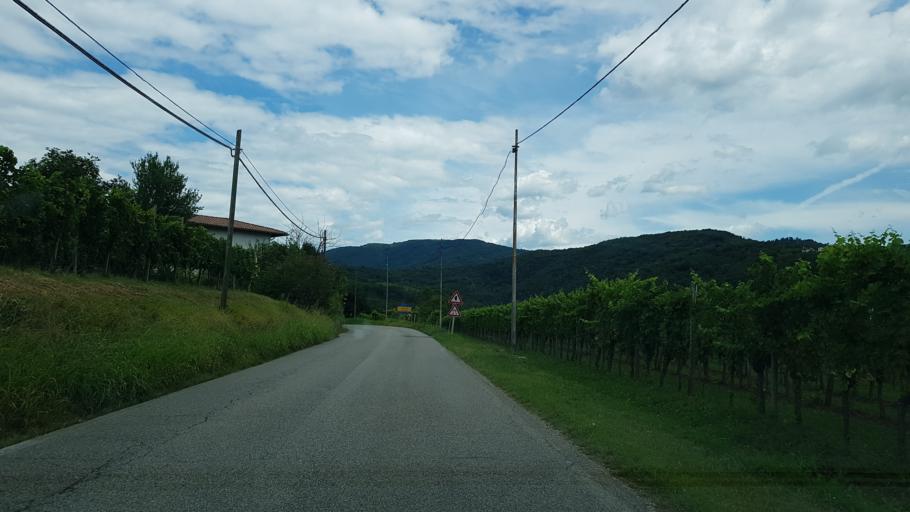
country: IT
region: Friuli Venezia Giulia
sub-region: Provincia di Udine
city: Prepotto
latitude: 46.0514
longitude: 13.4865
